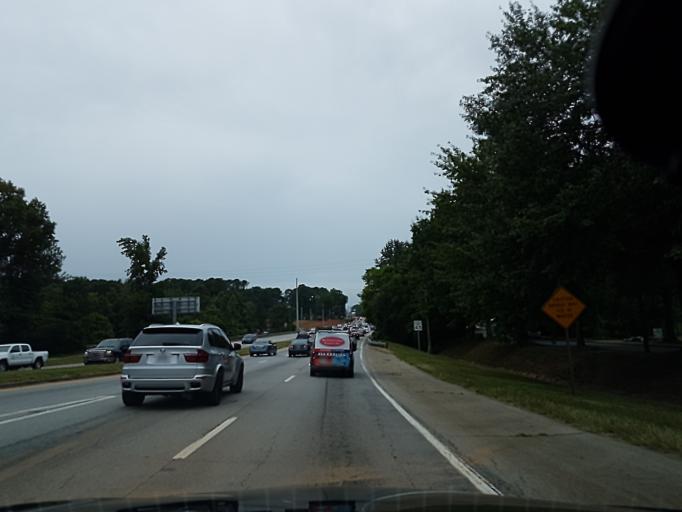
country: US
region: Georgia
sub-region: DeKalb County
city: Scottdale
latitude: 33.8053
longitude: -84.2758
